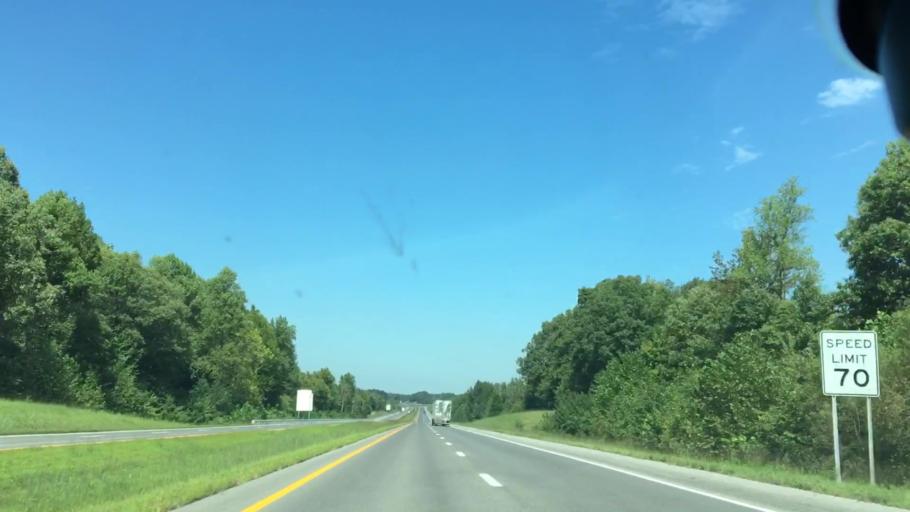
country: US
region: Kentucky
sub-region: Webster County
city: Sebree
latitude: 37.4991
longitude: -87.4751
